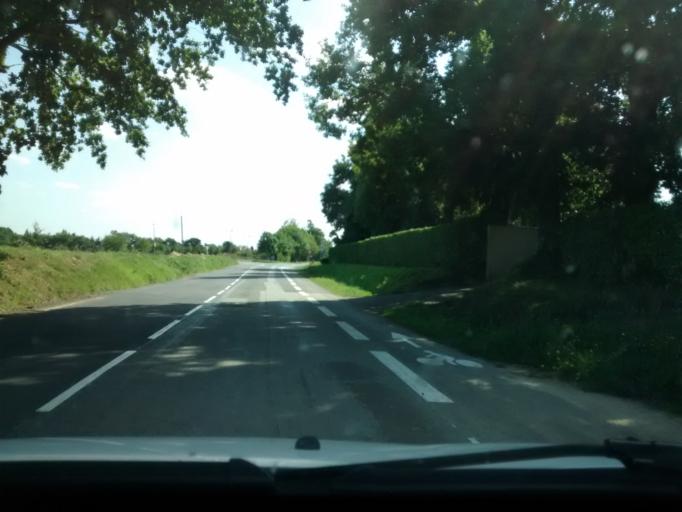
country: FR
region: Brittany
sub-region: Departement d'Ille-et-Vilaine
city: Cesson-Sevigne
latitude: 48.1313
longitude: -1.6152
